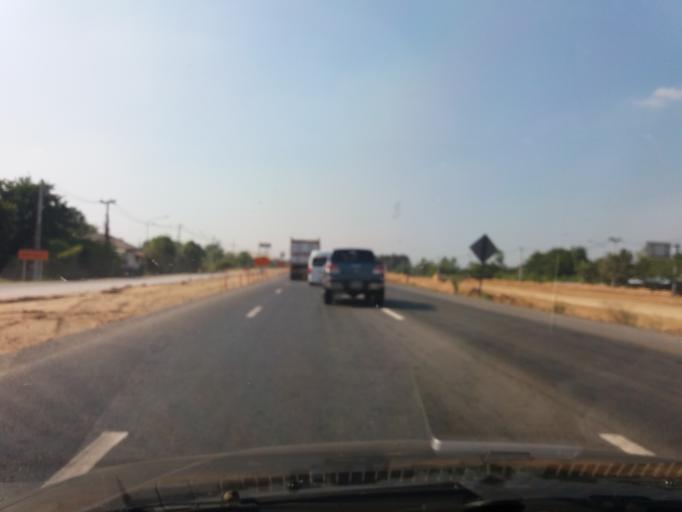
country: TH
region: Nakhon Sawan
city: Nakhon Sawan
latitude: 15.6364
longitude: 100.0974
